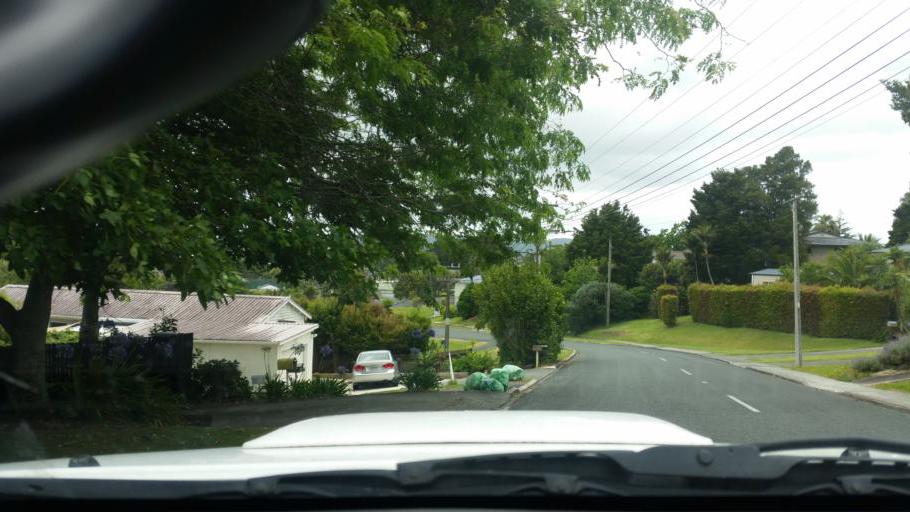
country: NZ
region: Northland
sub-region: Whangarei
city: Ruakaka
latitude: -36.1139
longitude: 174.3500
